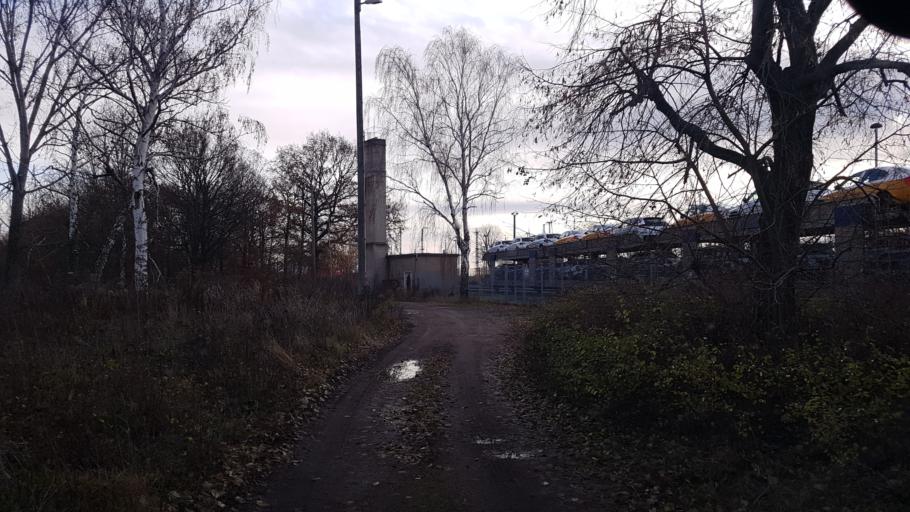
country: DE
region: Brandenburg
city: Falkenberg
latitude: 51.5847
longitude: 13.2766
